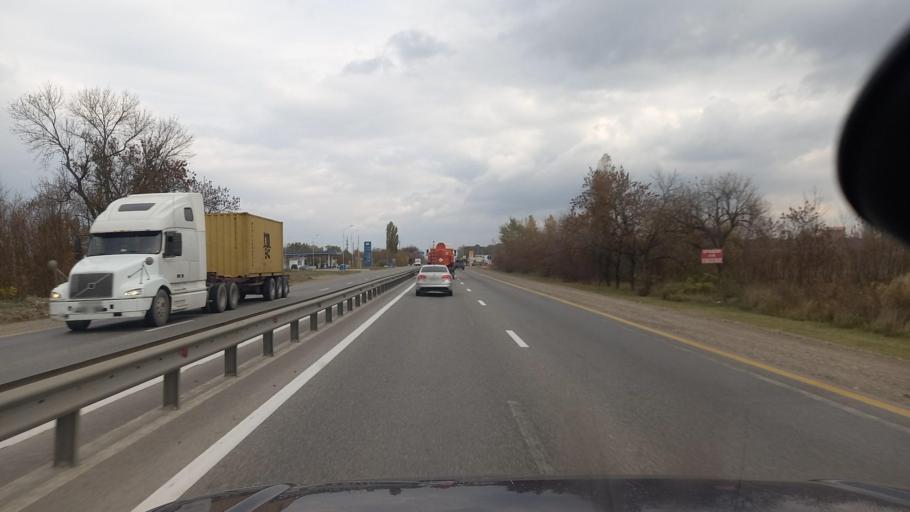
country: RU
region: Krasnodarskiy
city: Afipskiy
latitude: 44.8999
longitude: 38.8689
